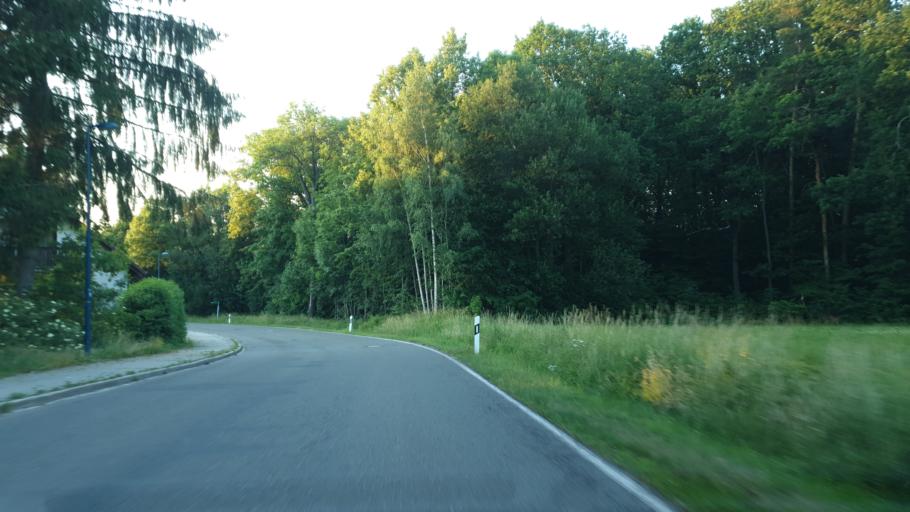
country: DE
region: Saxony
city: Oelsnitz
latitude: 50.7116
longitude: 12.7092
